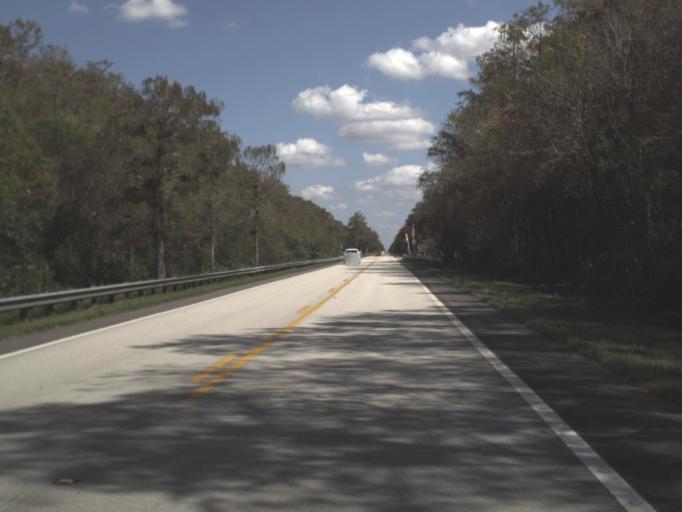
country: US
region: Florida
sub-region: Miami-Dade County
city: Kendall West
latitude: 25.8557
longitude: -81.0220
